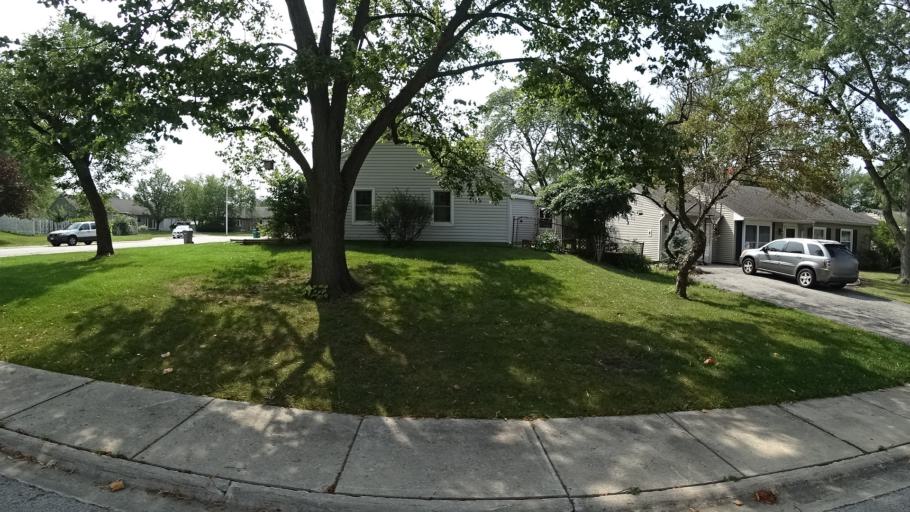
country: US
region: Illinois
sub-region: Cook County
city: Orland Park
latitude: 41.6176
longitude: -87.8685
